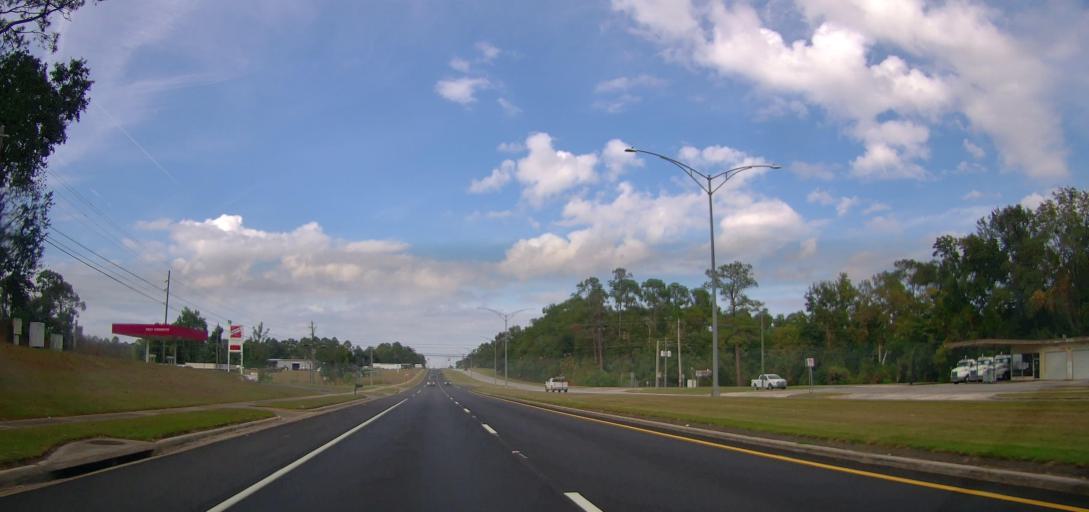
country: US
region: Georgia
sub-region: Mitchell County
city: Pelham
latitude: 31.1228
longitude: -84.1402
